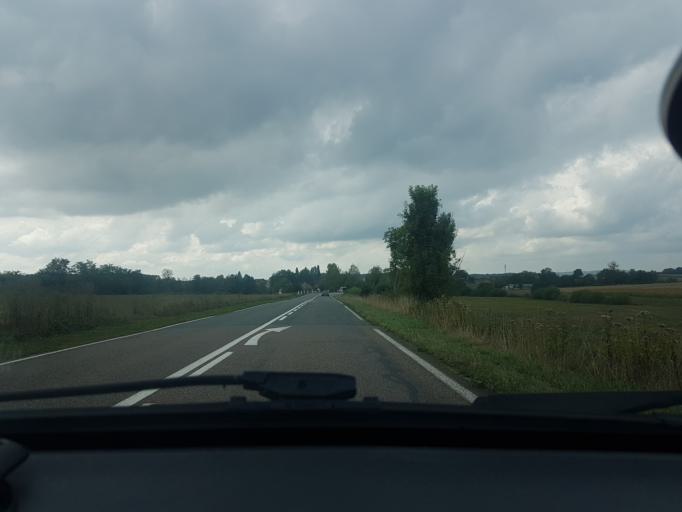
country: FR
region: Franche-Comte
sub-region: Departement de la Haute-Saone
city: Villersexel
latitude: 47.5429
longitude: 6.4943
